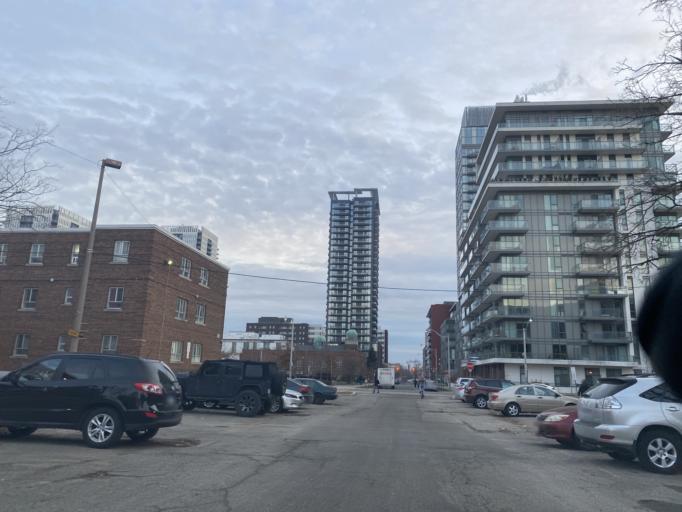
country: CA
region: Ontario
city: Toronto
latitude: 43.6619
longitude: -79.3637
